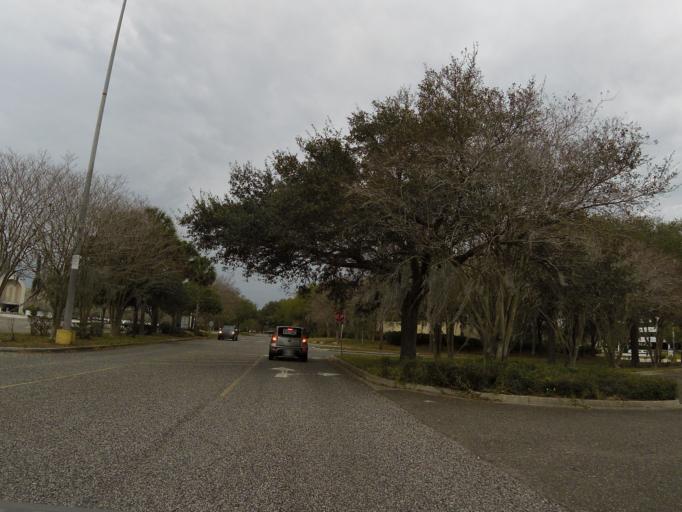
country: US
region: Florida
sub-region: Duval County
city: Jacksonville
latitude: 30.3252
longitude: -81.5514
